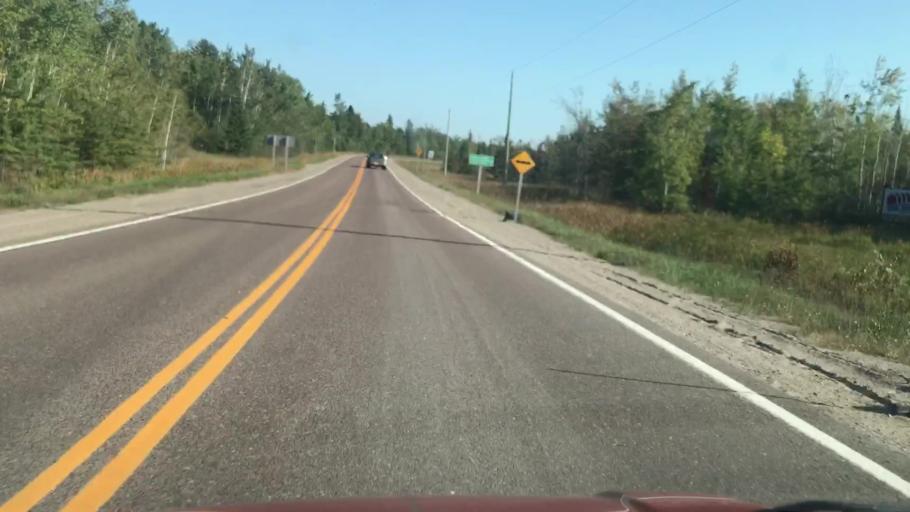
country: CA
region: Ontario
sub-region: Algoma
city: Sault Ste. Marie
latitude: 46.3364
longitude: -84.0088
